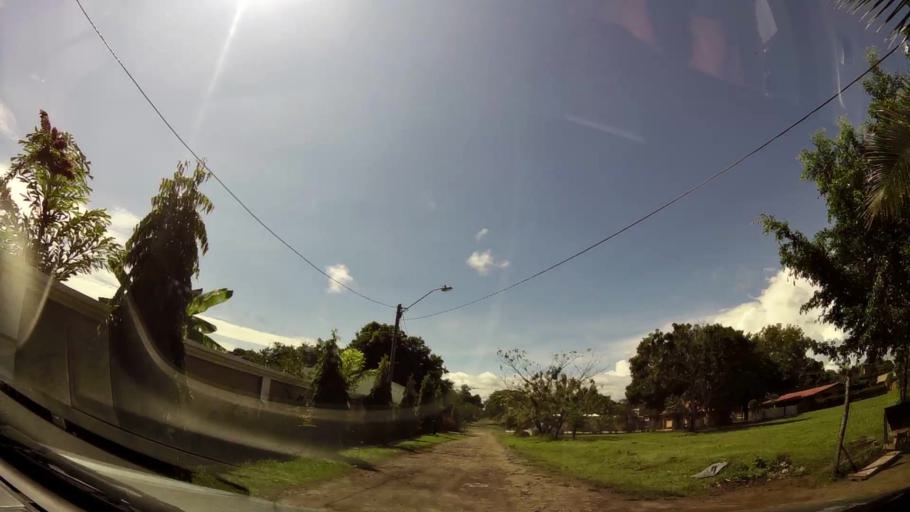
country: PA
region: Panama
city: Nueva Gorgona
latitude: 8.5564
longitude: -79.8721
